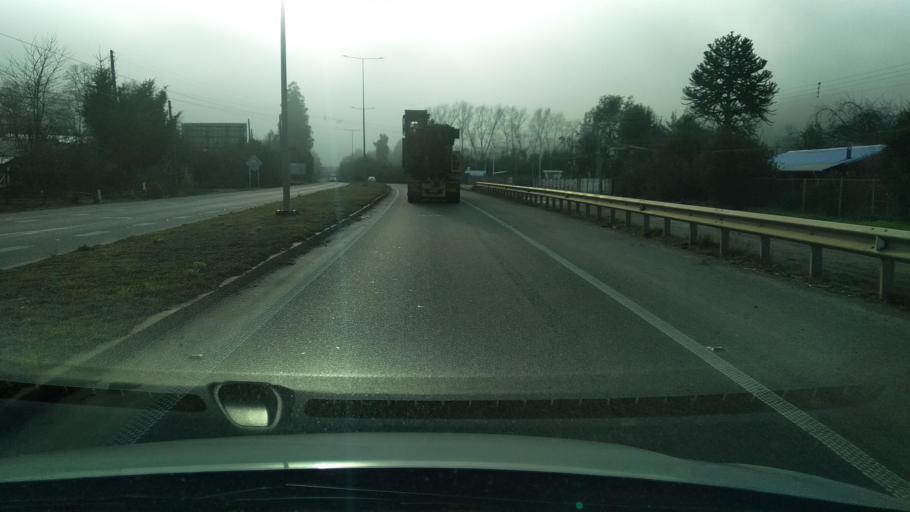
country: CL
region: Los Lagos
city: Las Animas
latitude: -39.7713
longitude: -73.2205
